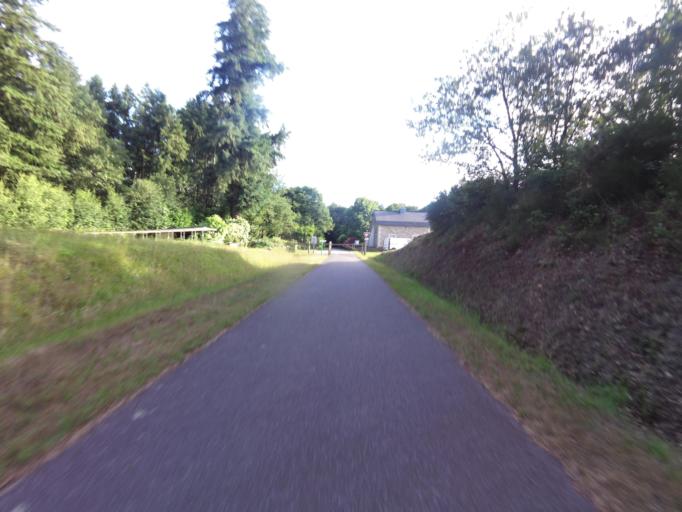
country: FR
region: Brittany
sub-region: Departement du Morbihan
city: Ploermel
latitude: 47.9196
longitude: -2.4266
